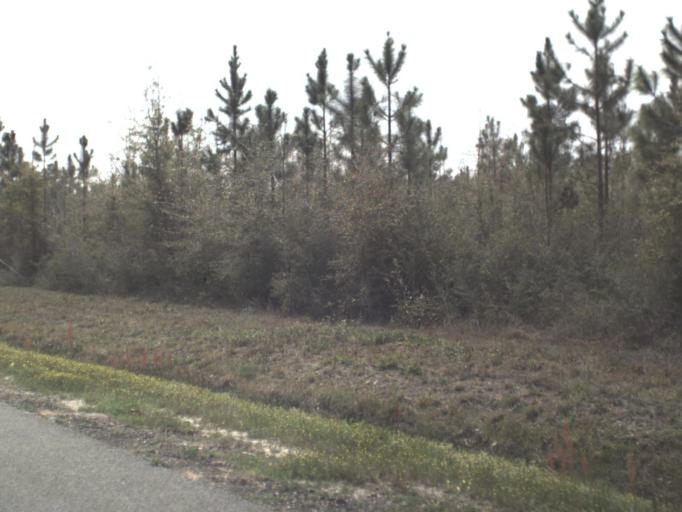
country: US
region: Florida
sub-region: Gulf County
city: Wewahitchka
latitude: 30.0505
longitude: -85.1874
